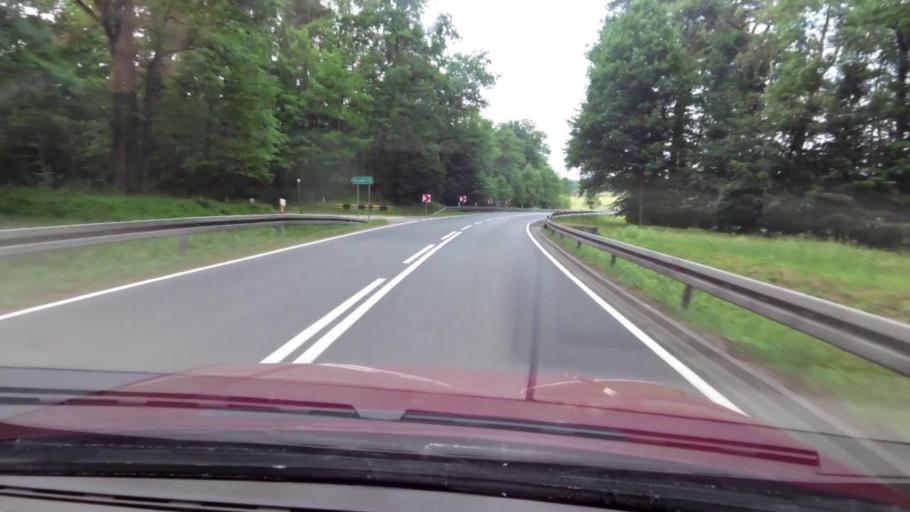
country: PL
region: Pomeranian Voivodeship
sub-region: Powiat bytowski
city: Trzebielino
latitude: 54.2300
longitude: 17.0865
